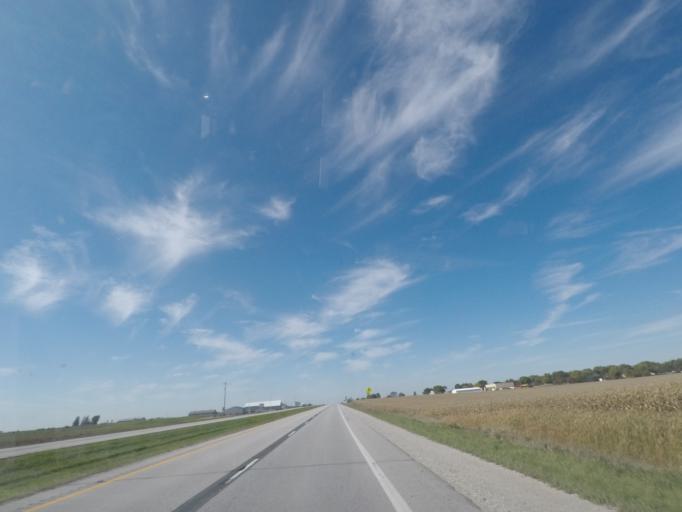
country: US
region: Iowa
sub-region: Story County
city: Nevada
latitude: 42.0079
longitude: -93.3109
